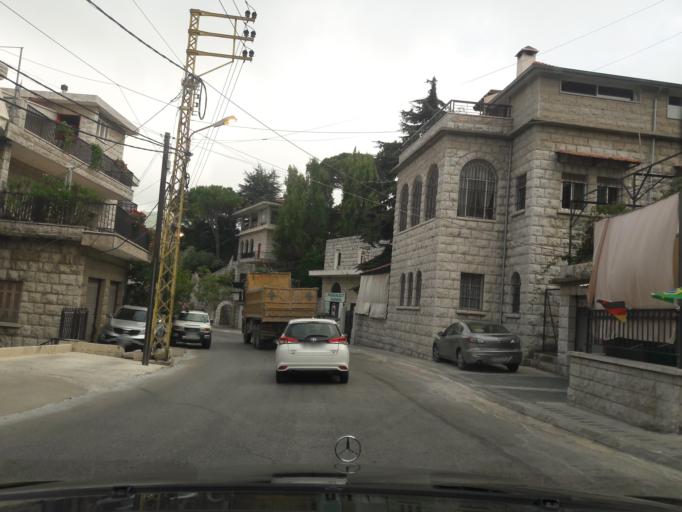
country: LB
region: Mont-Liban
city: Djounie
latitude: 33.9307
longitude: 35.7283
